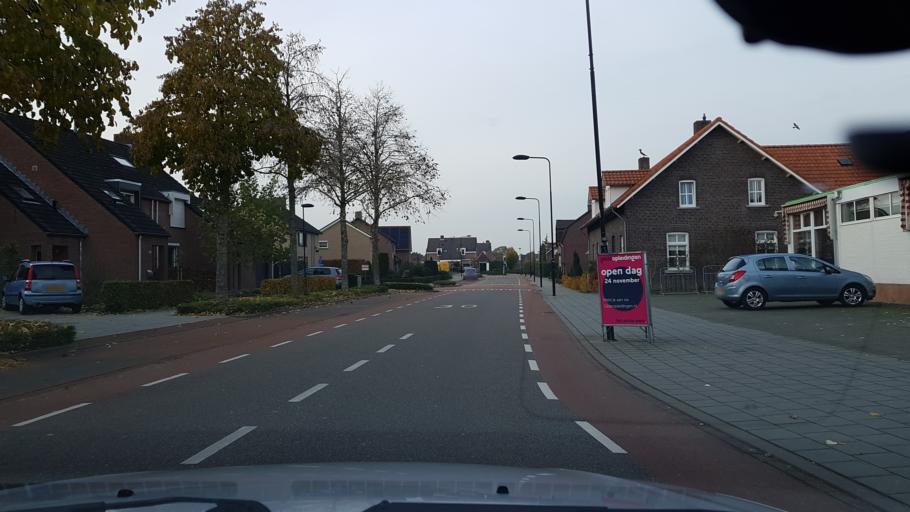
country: NL
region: Limburg
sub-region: Gemeente Beesel
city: Reuver
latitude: 51.2804
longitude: 6.0696
